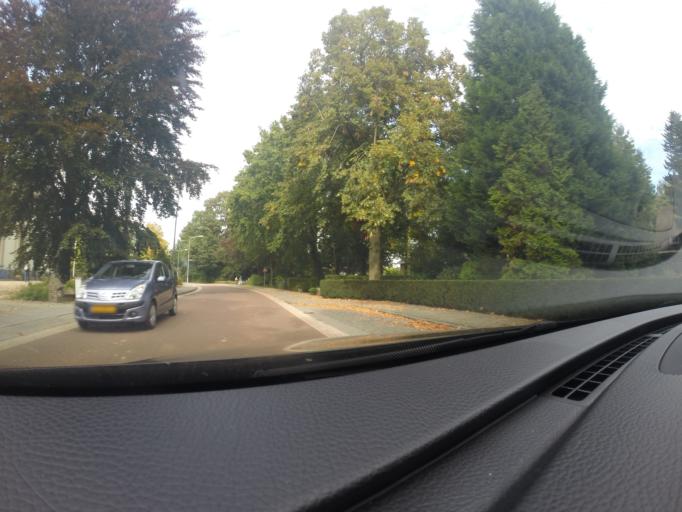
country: NL
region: Gelderland
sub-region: Gemeente Doetinchem
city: Doetinchem
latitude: 51.9636
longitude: 6.2125
